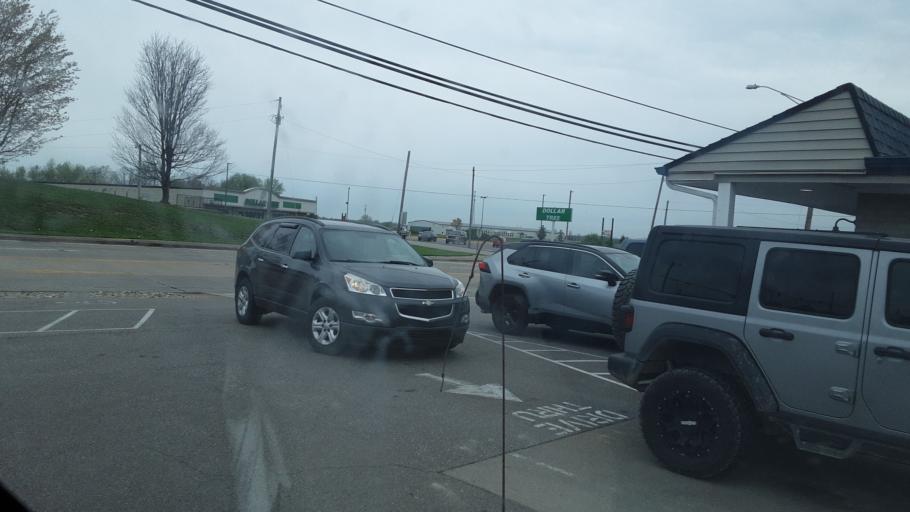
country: US
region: Kentucky
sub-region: Grant County
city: Dry Ridge
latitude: 38.6831
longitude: -84.6071
